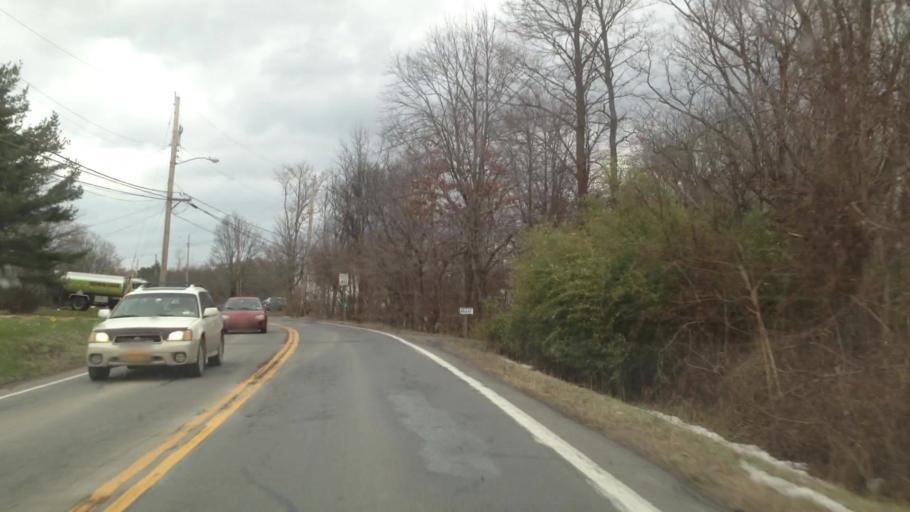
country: US
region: New York
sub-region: Ulster County
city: Glasco
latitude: 42.0252
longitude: -73.9543
